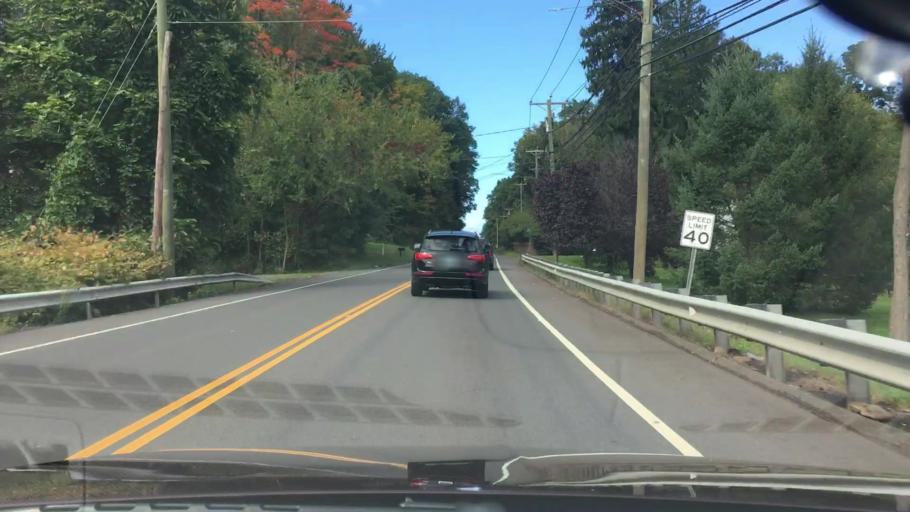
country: US
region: Connecticut
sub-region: Hartford County
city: Kensington
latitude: 41.6097
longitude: -72.7201
